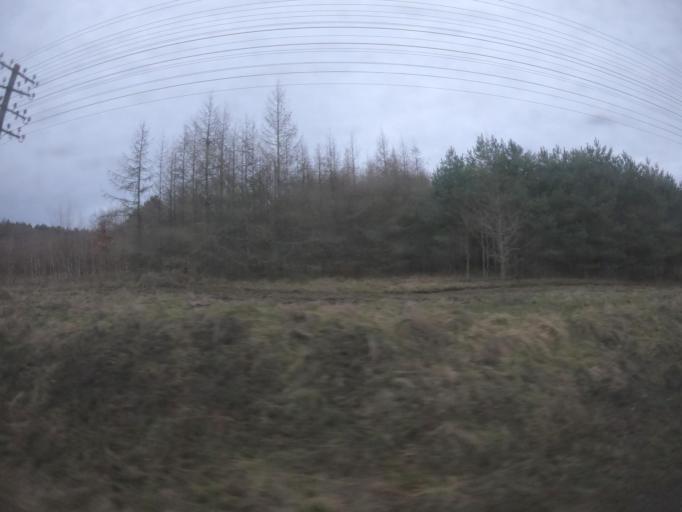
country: PL
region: West Pomeranian Voivodeship
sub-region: Powiat szczecinecki
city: Borne Sulinowo
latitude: 53.6584
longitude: 16.5652
